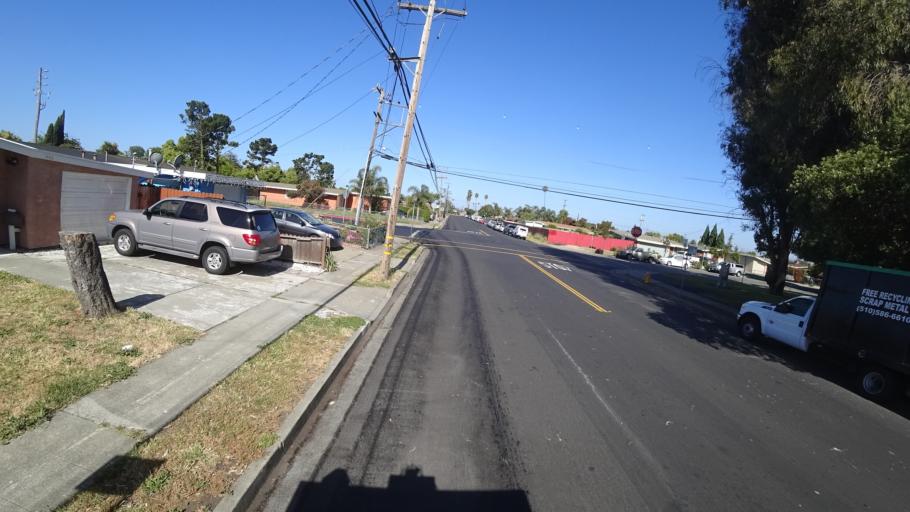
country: US
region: California
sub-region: Alameda County
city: Hayward
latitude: 37.6243
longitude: -122.0748
